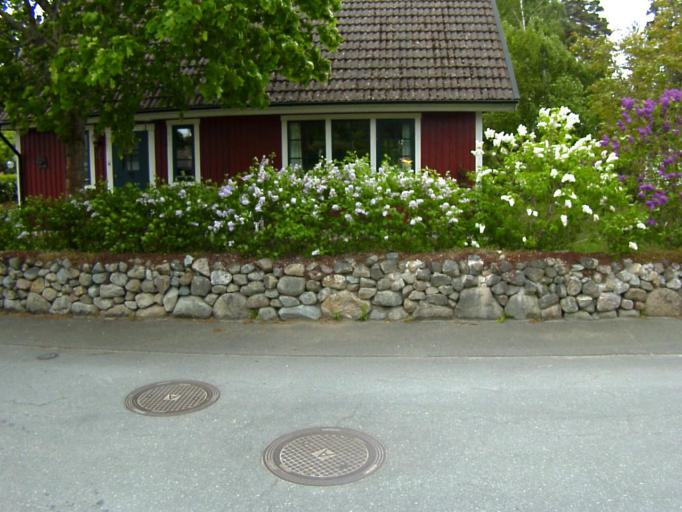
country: SE
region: Skane
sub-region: Kristianstads Kommun
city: Ahus
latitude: 55.9422
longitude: 14.2731
